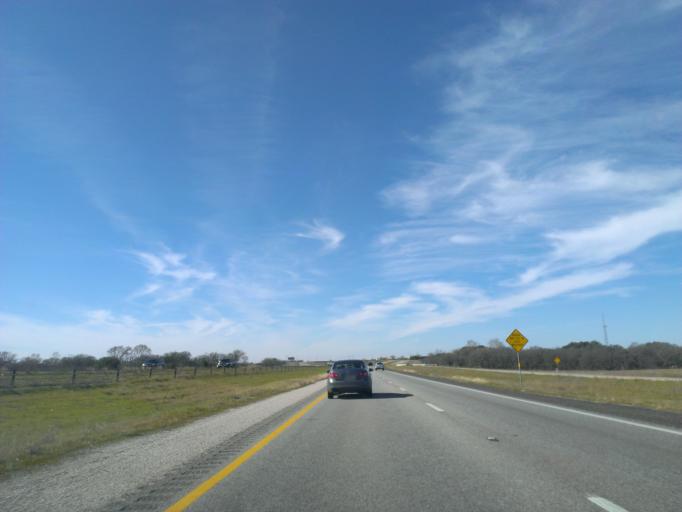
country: US
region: Texas
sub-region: Bell County
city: Nolanville
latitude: 31.0654
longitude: -97.5750
